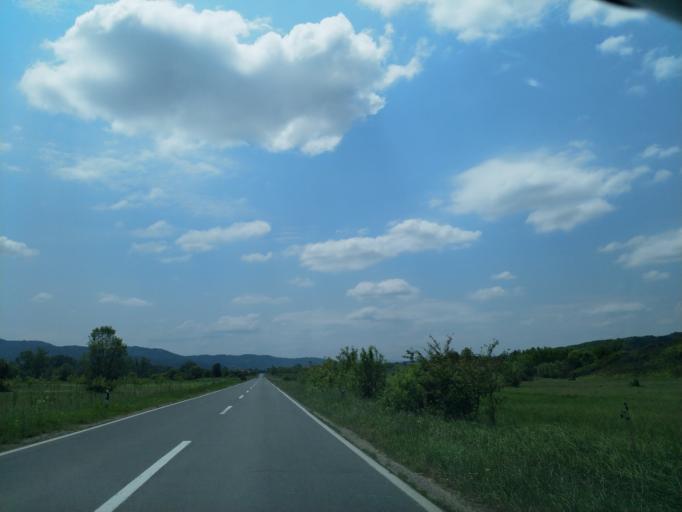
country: RS
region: Central Serbia
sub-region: Rasinski Okrug
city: Krusevac
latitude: 43.4591
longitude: 21.2445
